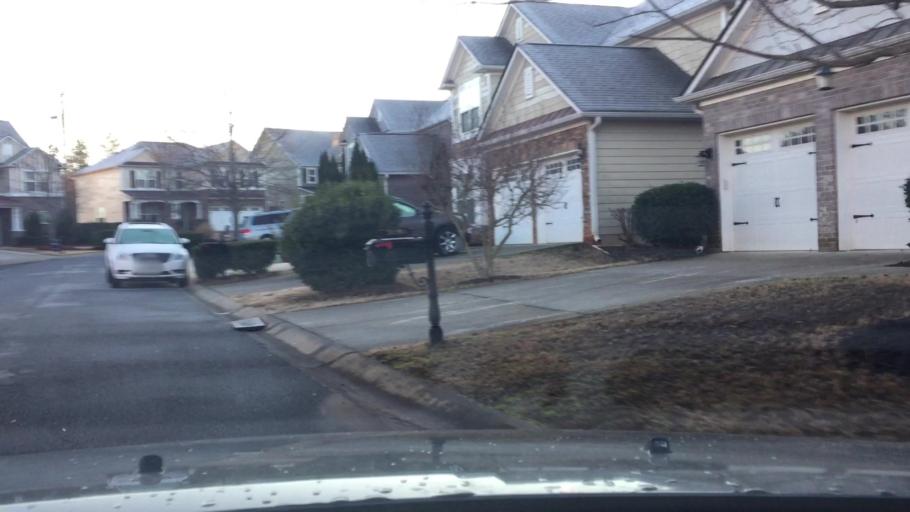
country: US
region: Georgia
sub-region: Forsyth County
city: Cumming
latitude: 34.1776
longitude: -84.1941
